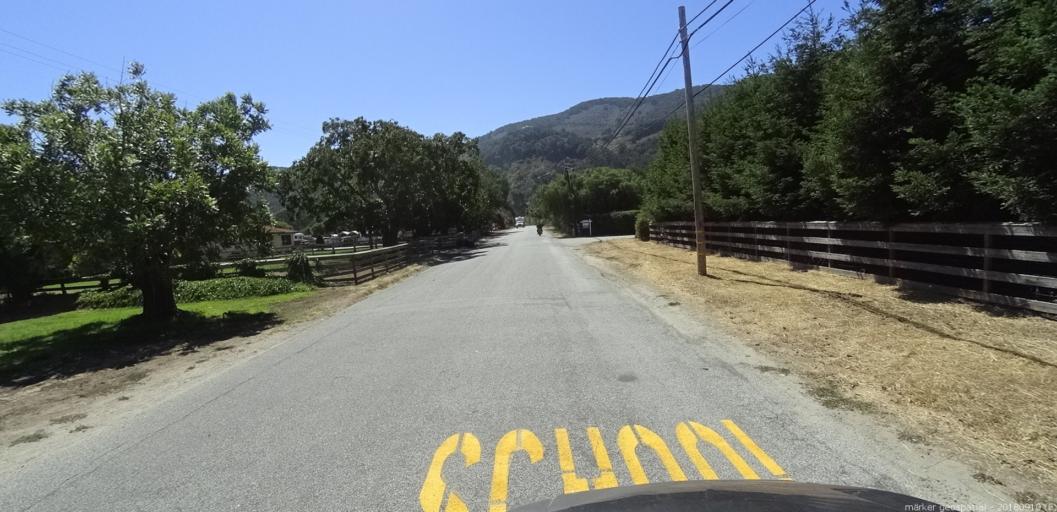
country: US
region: California
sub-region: Monterey County
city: Del Rey Oaks
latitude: 36.5289
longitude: -121.8307
